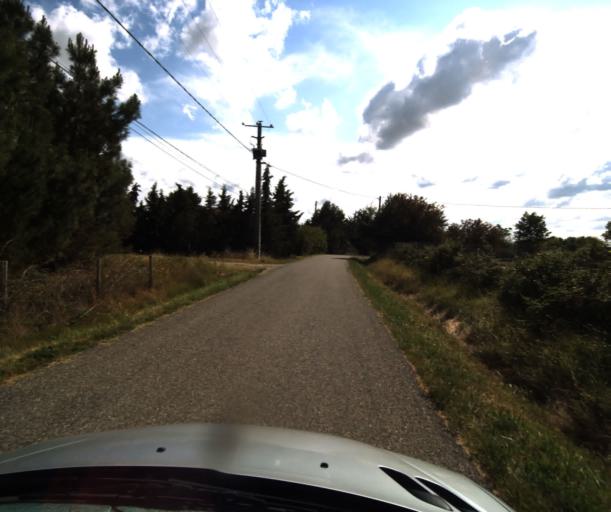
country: FR
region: Midi-Pyrenees
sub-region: Departement du Tarn-et-Garonne
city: Campsas
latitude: 43.8960
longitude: 1.2974
